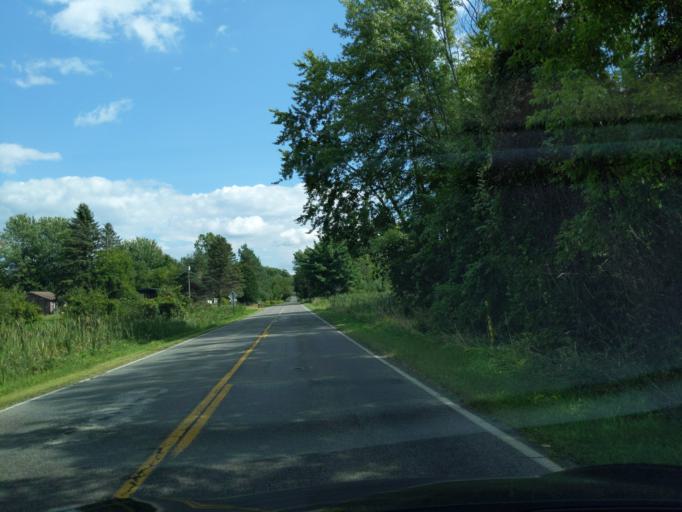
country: US
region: Michigan
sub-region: Jackson County
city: Spring Arbor
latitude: 42.3081
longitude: -84.5162
